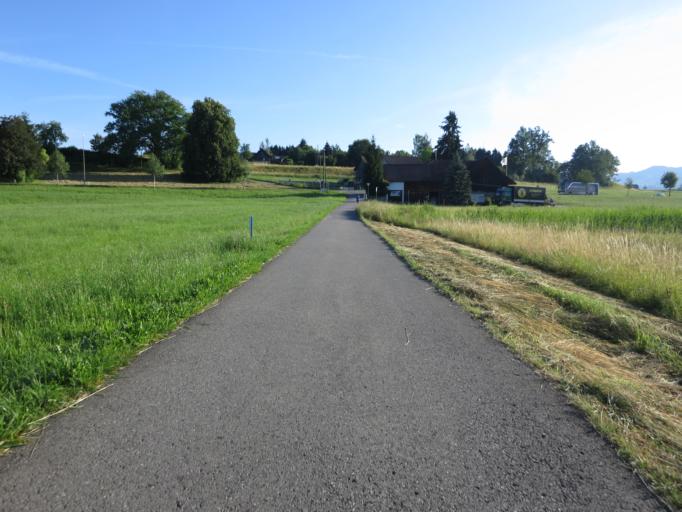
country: CH
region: Zurich
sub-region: Bezirk Hinwil
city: Bubikon
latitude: 47.2578
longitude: 8.8139
